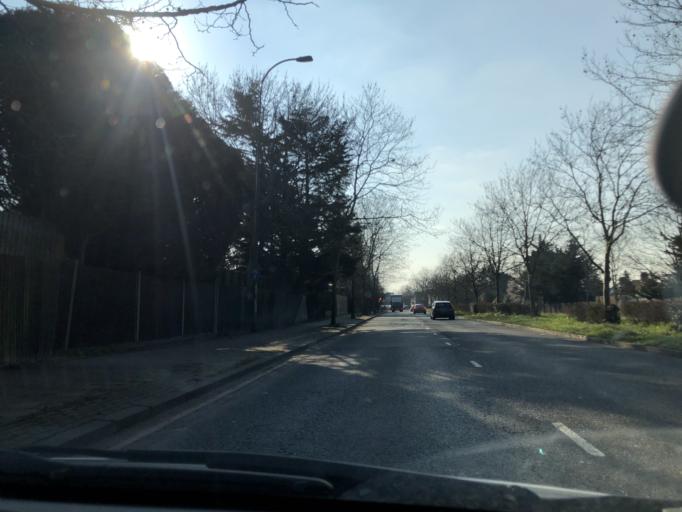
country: GB
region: England
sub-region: Greater London
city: Blackheath
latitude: 51.4472
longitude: 0.0190
